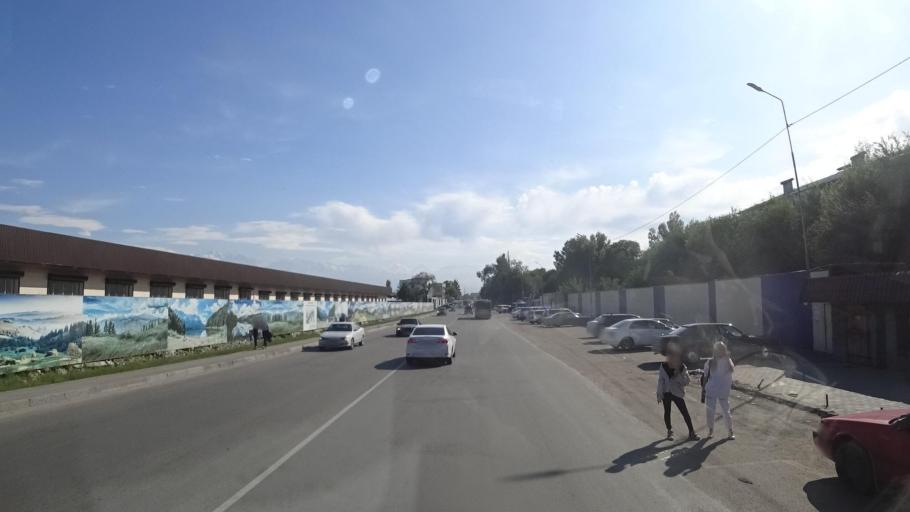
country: KZ
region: Almaty Oblysy
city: Energeticheskiy
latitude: 43.4199
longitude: 77.0221
